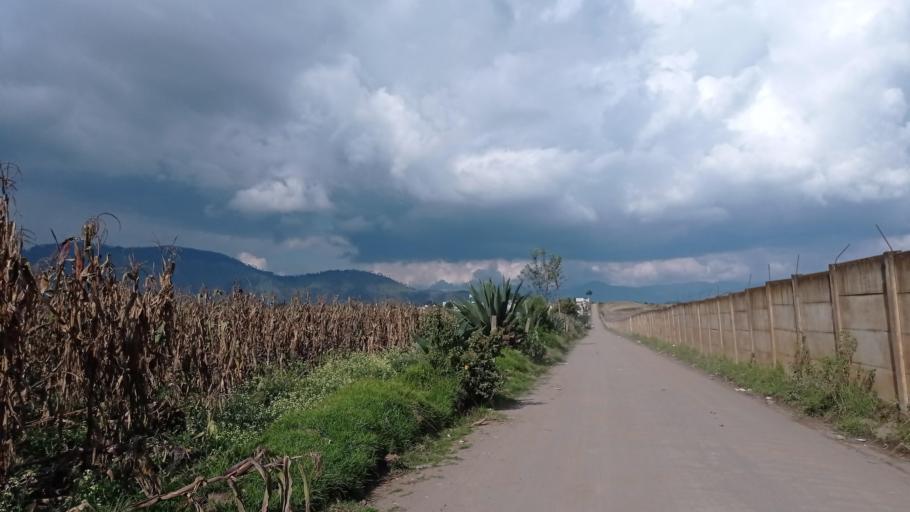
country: GT
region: Quetzaltenango
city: Olintepeque
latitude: 14.8650
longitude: -91.5053
